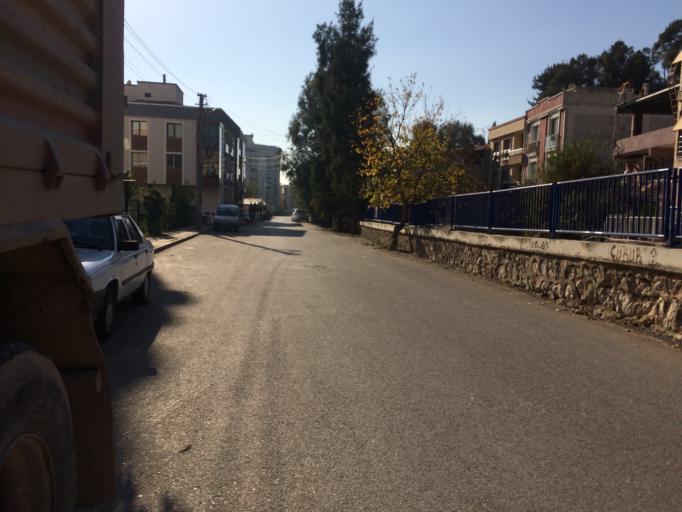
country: TR
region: Izmir
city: Karsiyaka
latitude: 38.4899
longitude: 27.0586
